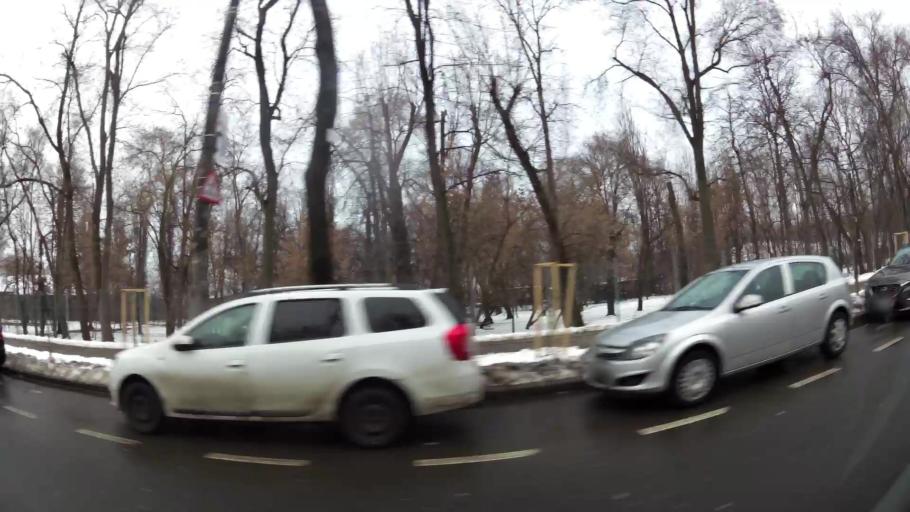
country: RO
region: Bucuresti
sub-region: Municipiul Bucuresti
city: Bucharest
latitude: 44.4787
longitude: 26.0875
